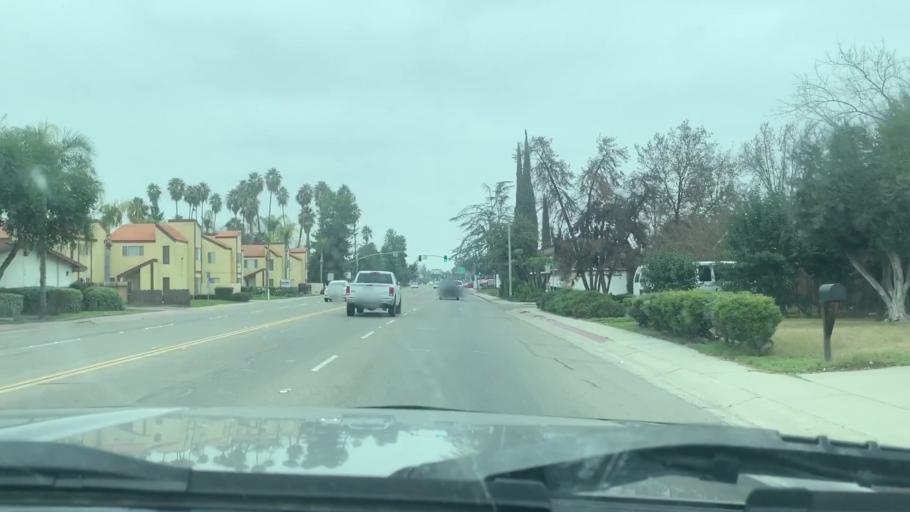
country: US
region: California
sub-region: Tulare County
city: Visalia
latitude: 36.3228
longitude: -119.3317
